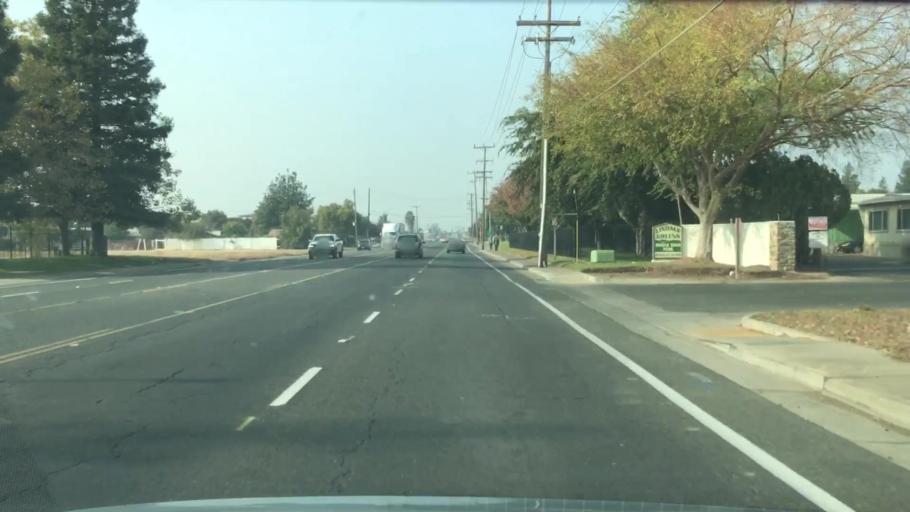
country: US
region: California
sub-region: Sacramento County
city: Florin
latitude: 38.4744
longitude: -121.4137
